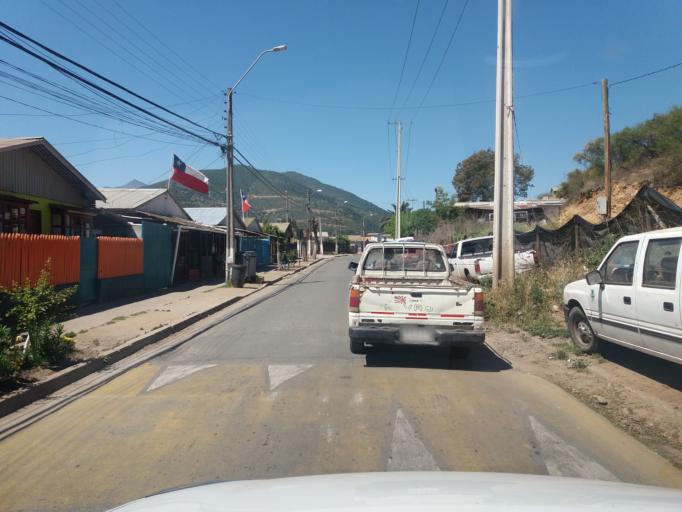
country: CL
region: Valparaiso
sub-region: Provincia de Quillota
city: Quillota
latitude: -32.9396
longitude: -71.2756
